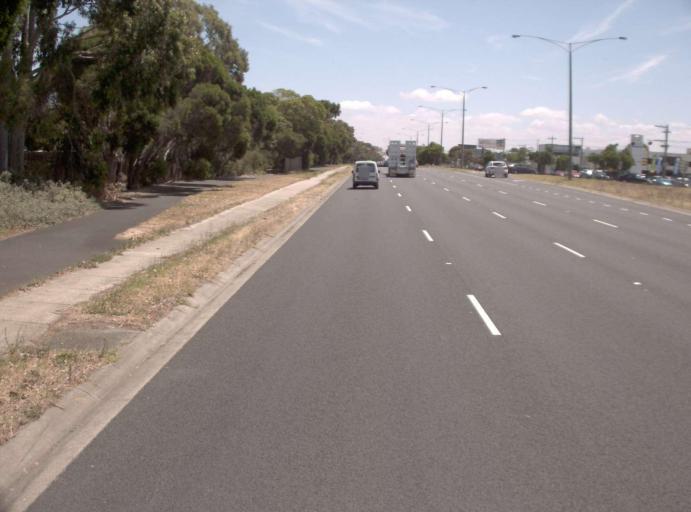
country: AU
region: Victoria
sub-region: Bayside
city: Hampton East
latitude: -37.9286
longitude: 145.0299
